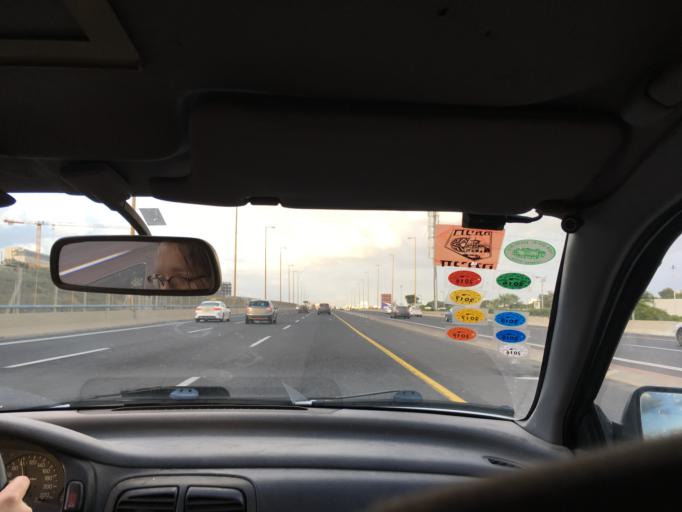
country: IL
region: Tel Aviv
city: Ramat Gan
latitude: 32.1038
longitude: 34.8050
